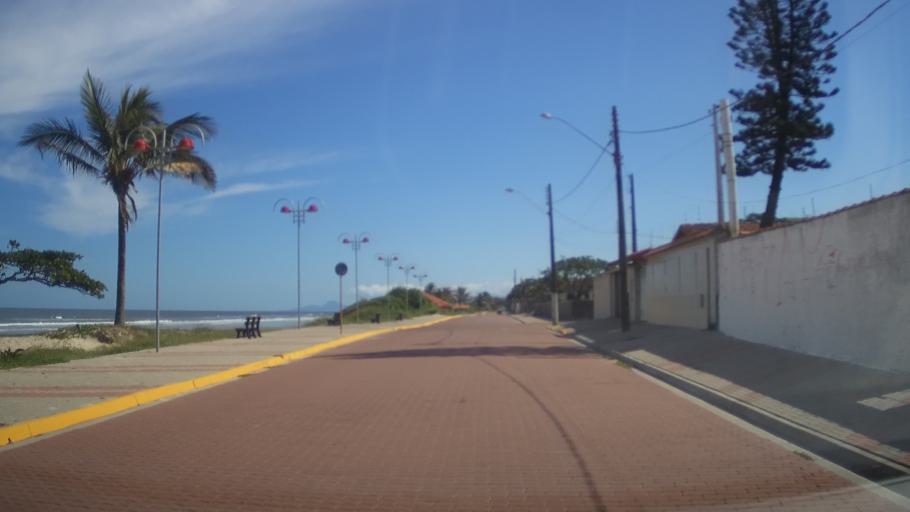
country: BR
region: Sao Paulo
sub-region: Itanhaem
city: Itanhaem
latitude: -24.1687
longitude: -46.7552
